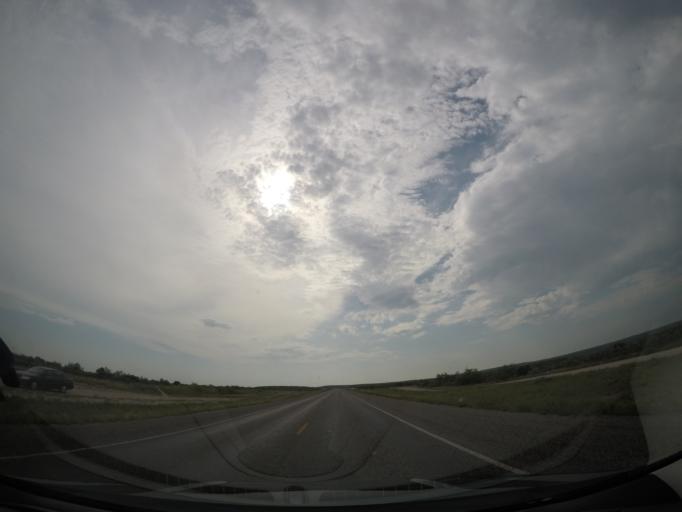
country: US
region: Texas
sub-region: Val Verde County
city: Cienegas Terrace
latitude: 29.7845
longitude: -101.4161
